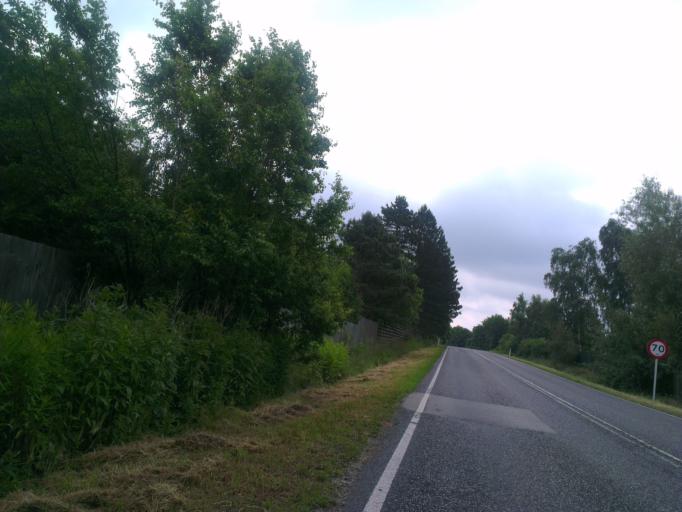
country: DK
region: Capital Region
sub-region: Frederikssund Kommune
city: Jaegerspris
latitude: 55.9080
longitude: 11.9368
